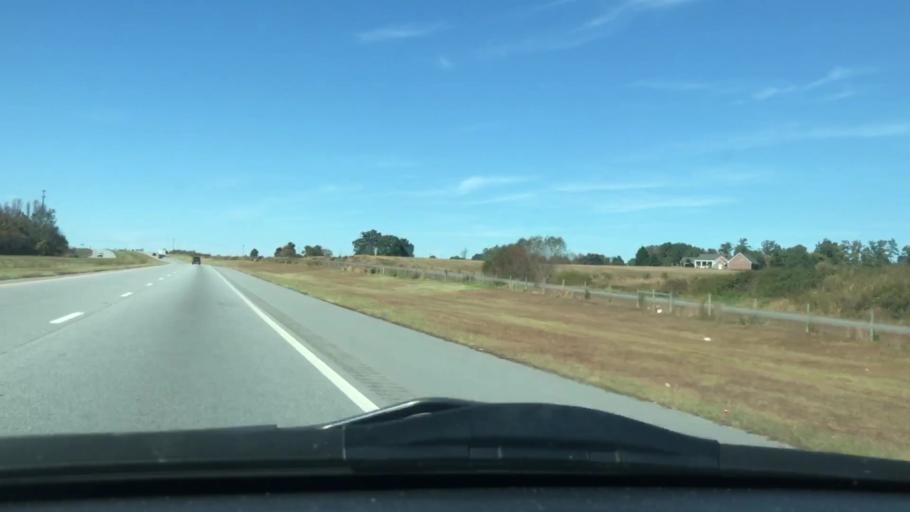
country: US
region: North Carolina
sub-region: Randolph County
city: Archdale
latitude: 35.8642
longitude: -79.8903
